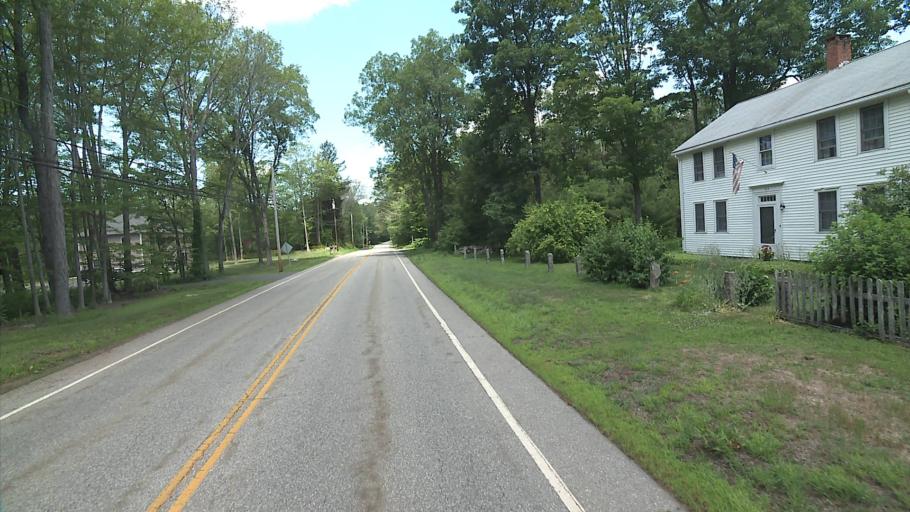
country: US
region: Connecticut
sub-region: Middlesex County
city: East Hampton
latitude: 41.5394
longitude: -72.5011
